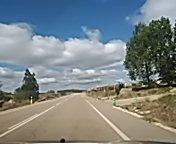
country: ES
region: Castille and Leon
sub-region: Provincia de Burgos
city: Hontoria del Pinar
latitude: 41.8510
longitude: -3.1734
